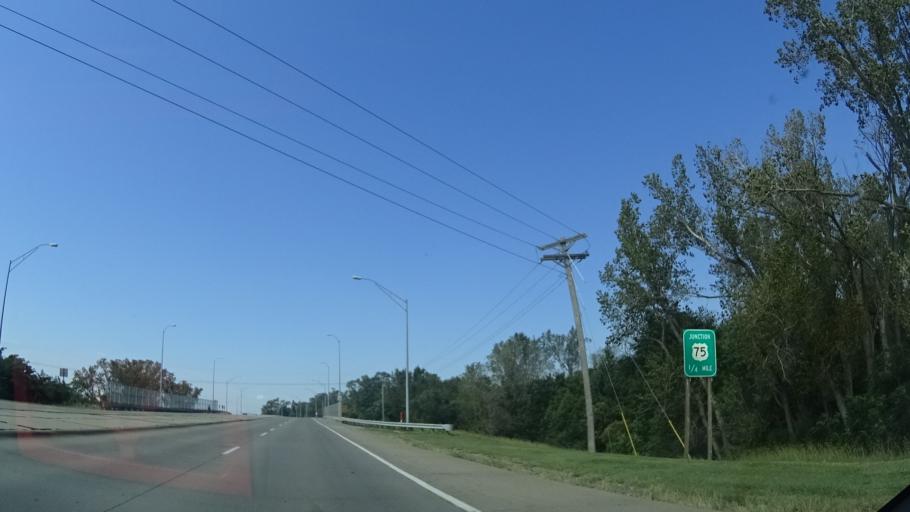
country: US
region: Nebraska
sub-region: Sarpy County
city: Offutt Air Force Base
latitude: 41.1158
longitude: -95.9286
